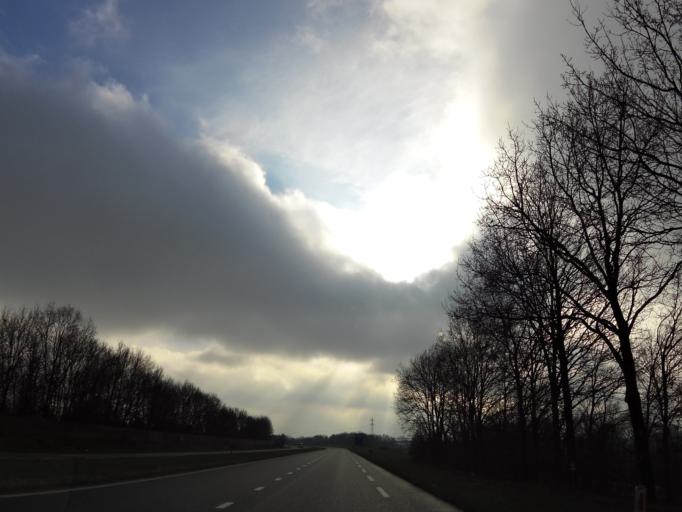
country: NL
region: Limburg
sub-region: Gemeente Gennep
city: Gennep
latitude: 51.7000
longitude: 5.9639
